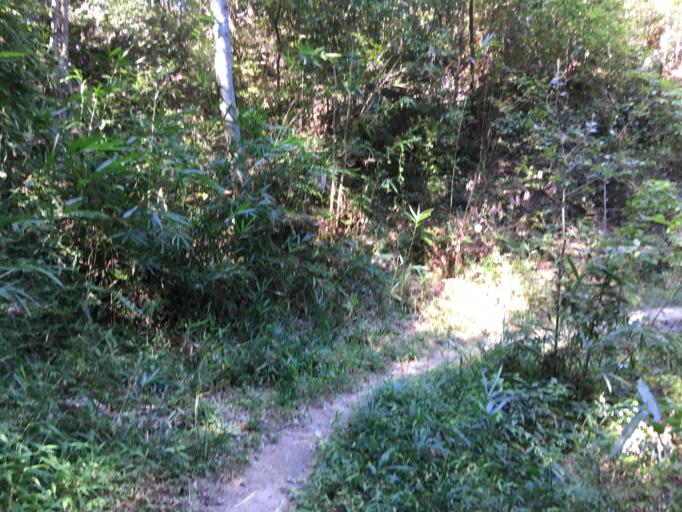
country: JP
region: Osaka
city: Neyagawa
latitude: 34.7435
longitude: 135.6835
